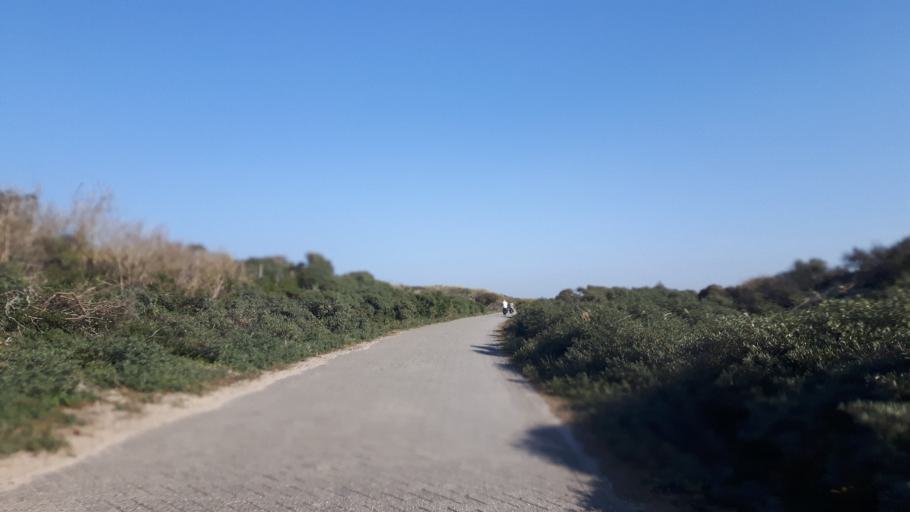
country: NL
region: South Holland
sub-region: Gemeente Noordwijkerhout
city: Noordwijkerhout
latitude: 52.2973
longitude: 4.4745
